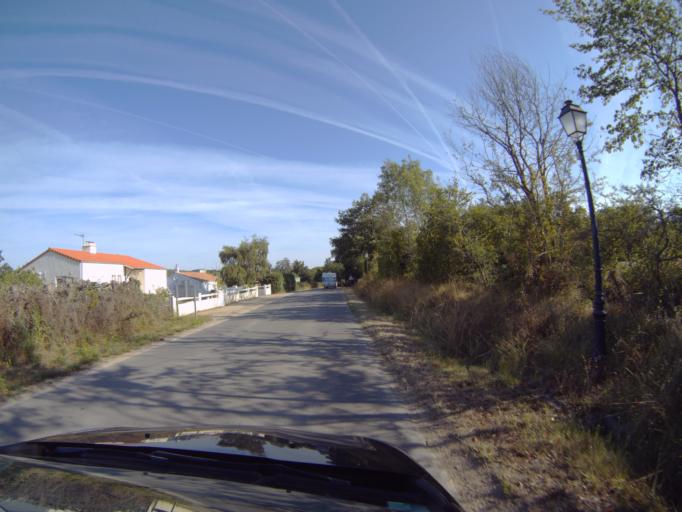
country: FR
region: Pays de la Loire
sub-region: Departement de la Vendee
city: Saint-Hilaire-de-Talmont
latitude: 46.4728
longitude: -1.6047
